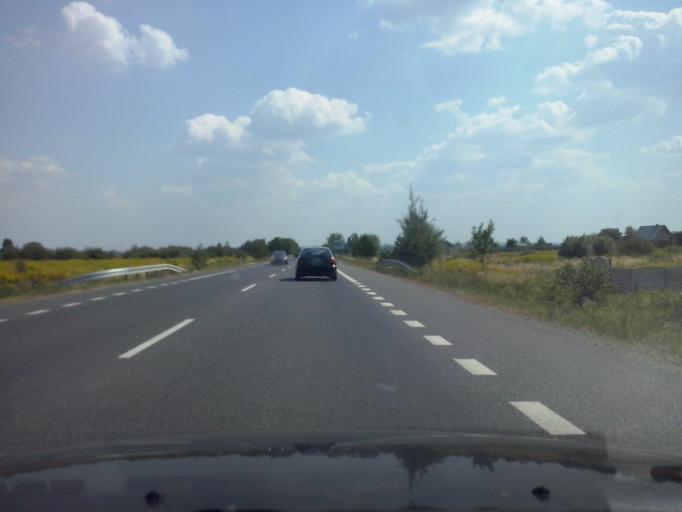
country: PL
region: Swietokrzyskie
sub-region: Powiat sandomierski
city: Loniow
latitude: 50.5521
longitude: 21.5395
